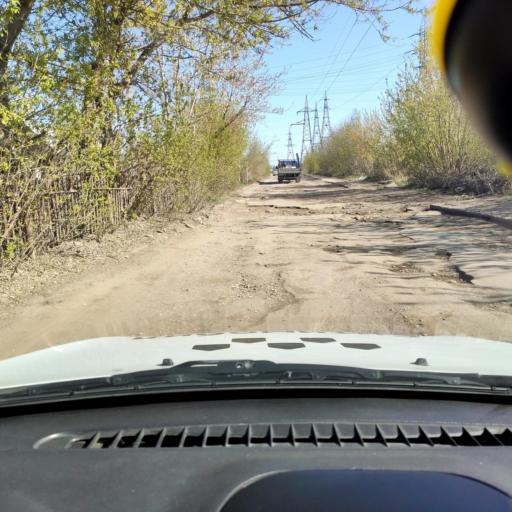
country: RU
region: Samara
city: Tol'yatti
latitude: 53.5863
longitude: 49.2950
